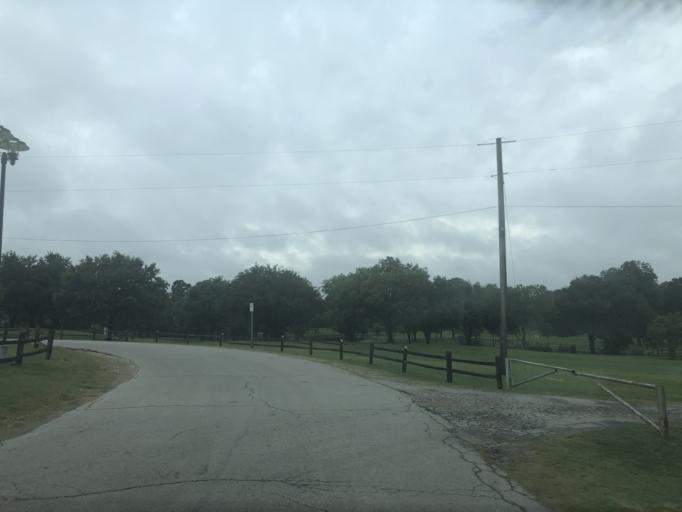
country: US
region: Texas
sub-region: Dallas County
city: Irving
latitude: 32.7969
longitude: -96.9399
